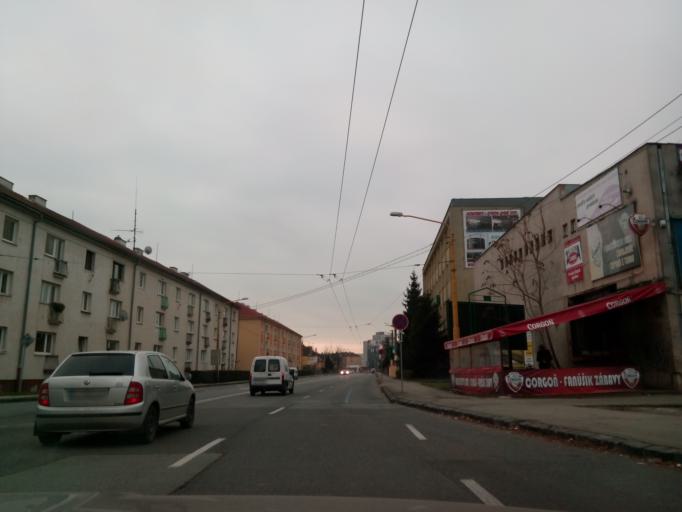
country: SK
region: Kosicky
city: Kosice
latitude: 48.7353
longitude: 21.2538
